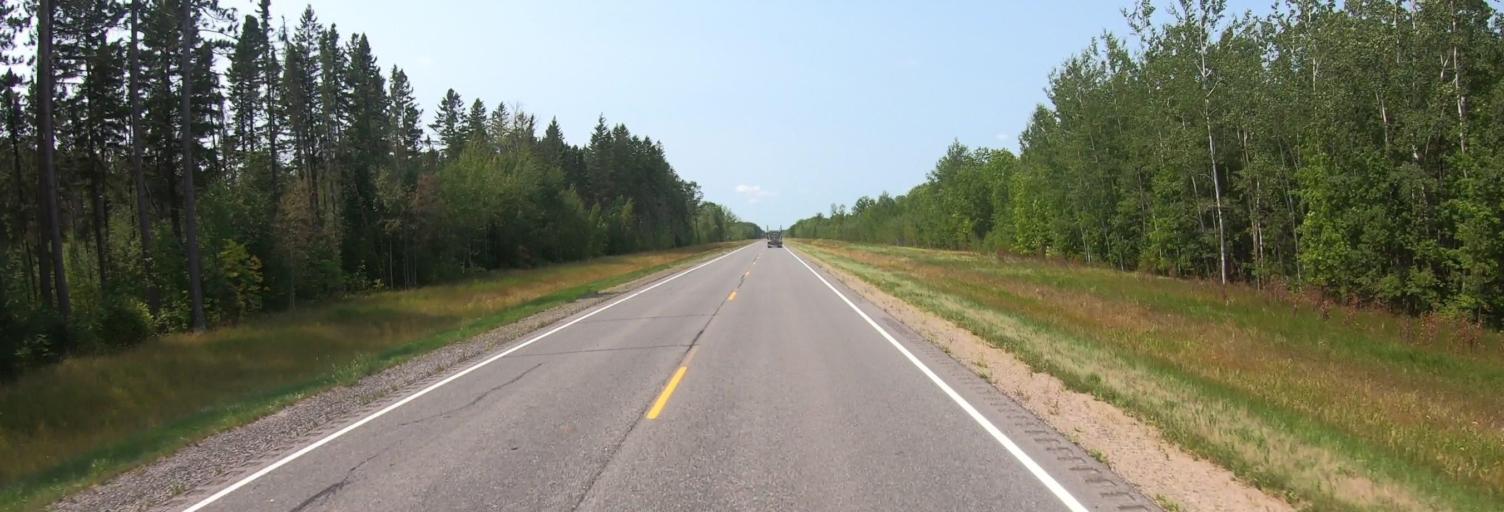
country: US
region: Minnesota
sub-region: Koochiching County
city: International Falls
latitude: 48.5127
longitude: -93.7346
